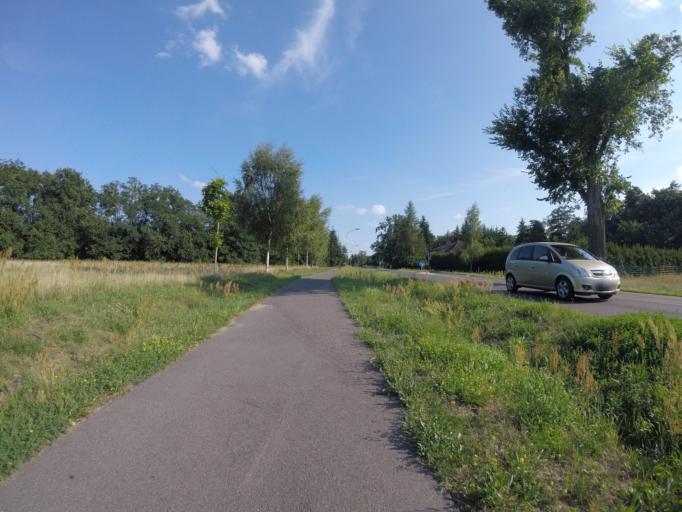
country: DE
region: Brandenburg
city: Bliesdorf
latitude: 52.6950
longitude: 14.1386
